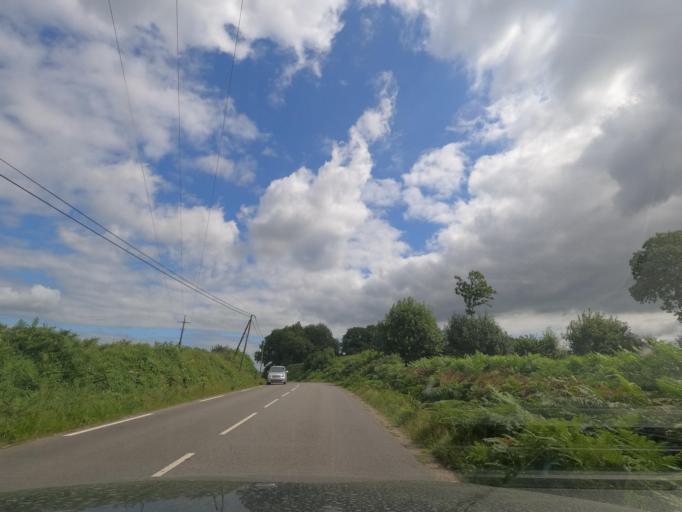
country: FR
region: Brittany
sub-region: Departement d'Ille-et-Vilaine
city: Louvigne-du-Desert
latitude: 48.4435
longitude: -1.0839
